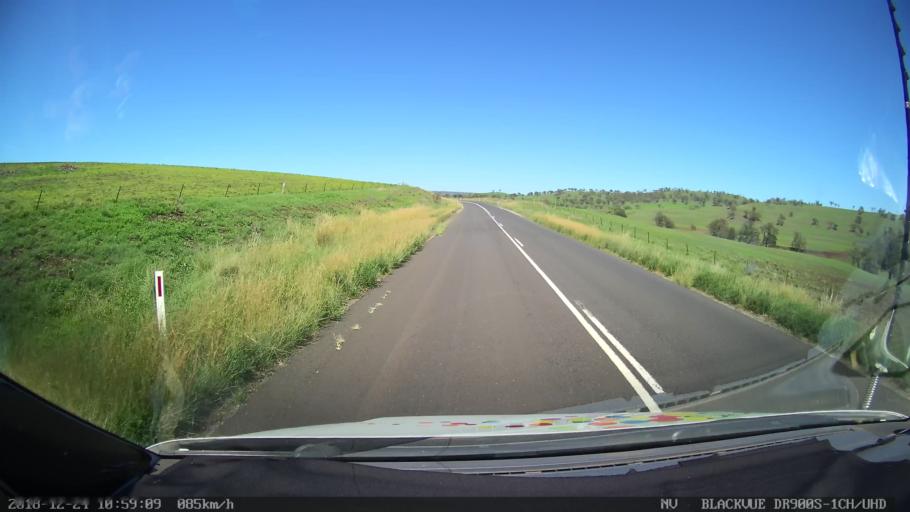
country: AU
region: New South Wales
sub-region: Upper Hunter Shire
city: Merriwa
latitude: -32.0539
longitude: 150.4027
